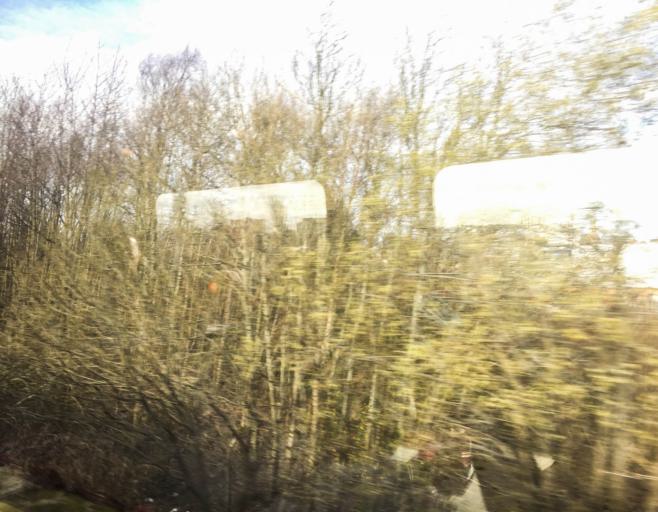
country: GB
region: Scotland
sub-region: North Lanarkshire
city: Coatbridge
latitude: 55.8575
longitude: -4.0255
